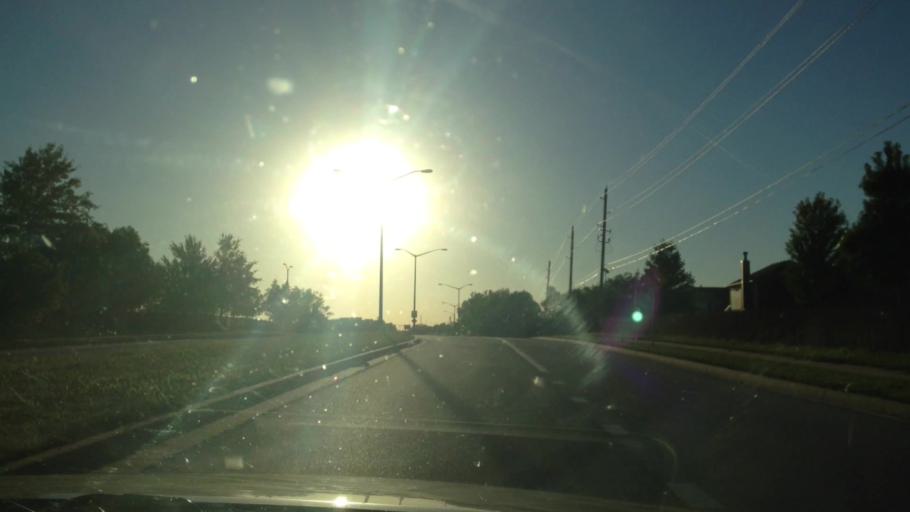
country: US
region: Missouri
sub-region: Clay County
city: Pleasant Valley
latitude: 39.2885
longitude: -94.4851
